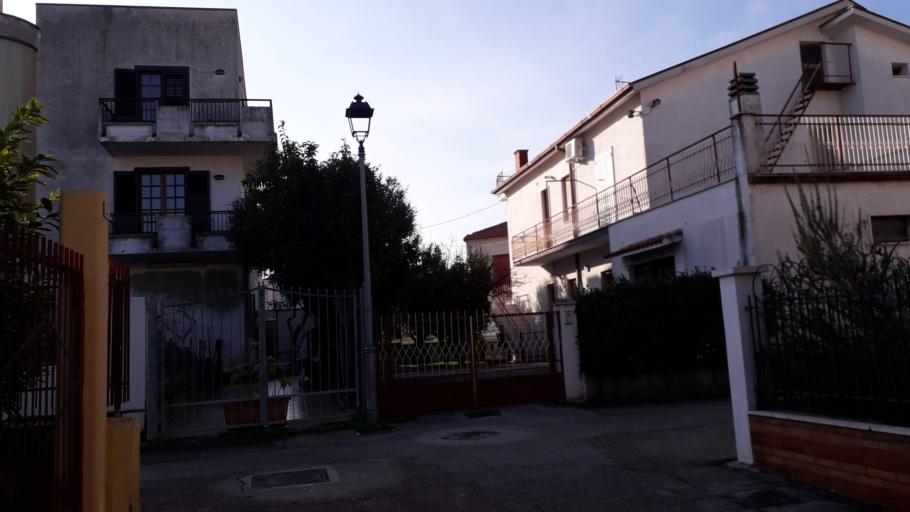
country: IT
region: Molise
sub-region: Provincia di Campobasso
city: Campomarino
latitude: 41.9570
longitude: 15.0318
